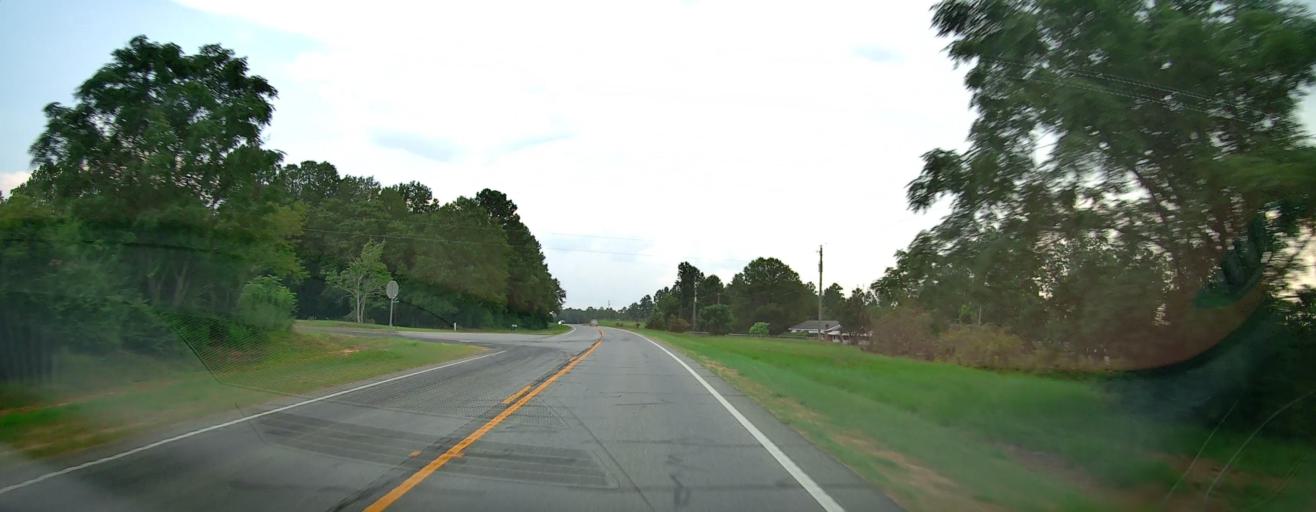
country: US
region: Georgia
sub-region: Laurens County
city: East Dublin
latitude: 32.5925
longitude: -82.8292
